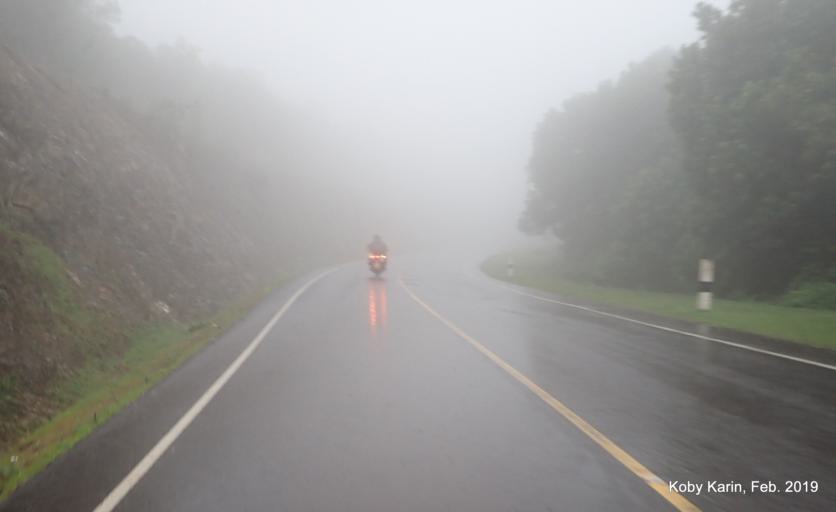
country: UG
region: Western Region
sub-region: Kisoro District
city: Kisoro
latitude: -1.2346
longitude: 29.8101
